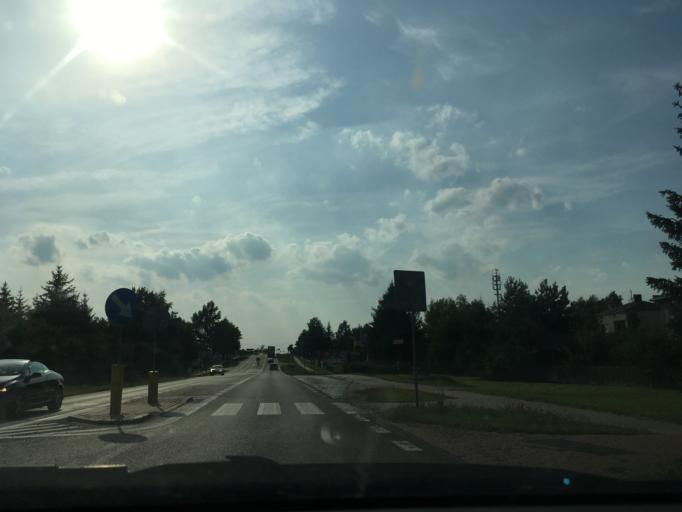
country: PL
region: Podlasie
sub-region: Powiat bialostocki
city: Wasilkow
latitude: 53.1253
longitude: 23.2537
